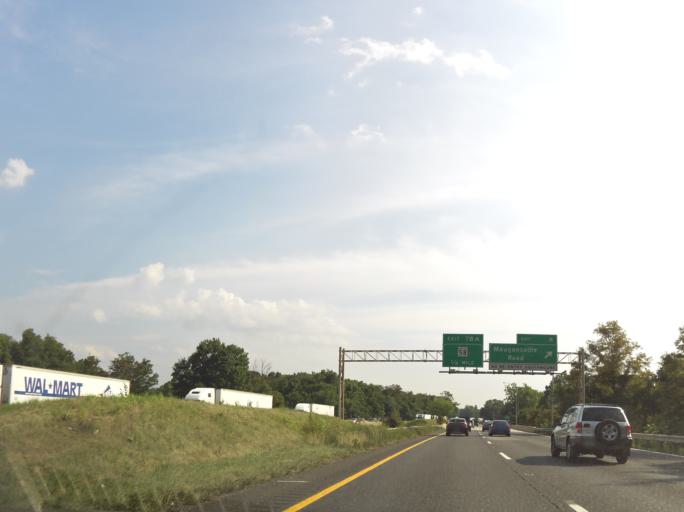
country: US
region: Maryland
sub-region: Washington County
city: Fountainhead-Orchard Hills
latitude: 39.6696
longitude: -77.7360
